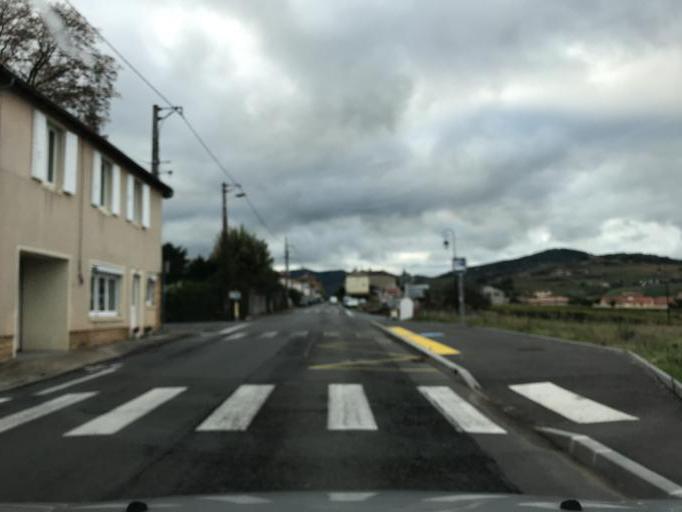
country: FR
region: Rhone-Alpes
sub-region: Departement du Rhone
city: Denice
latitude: 45.9986
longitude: 4.6465
